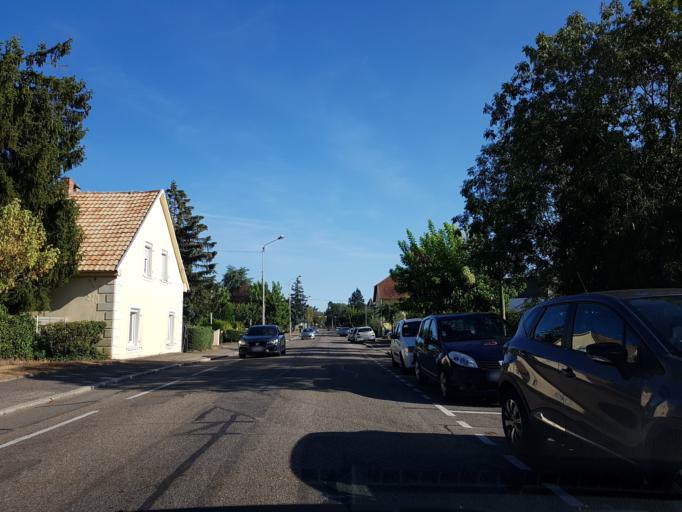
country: FR
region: Alsace
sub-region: Departement du Haut-Rhin
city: Pulversheim
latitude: 47.8368
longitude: 7.2993
